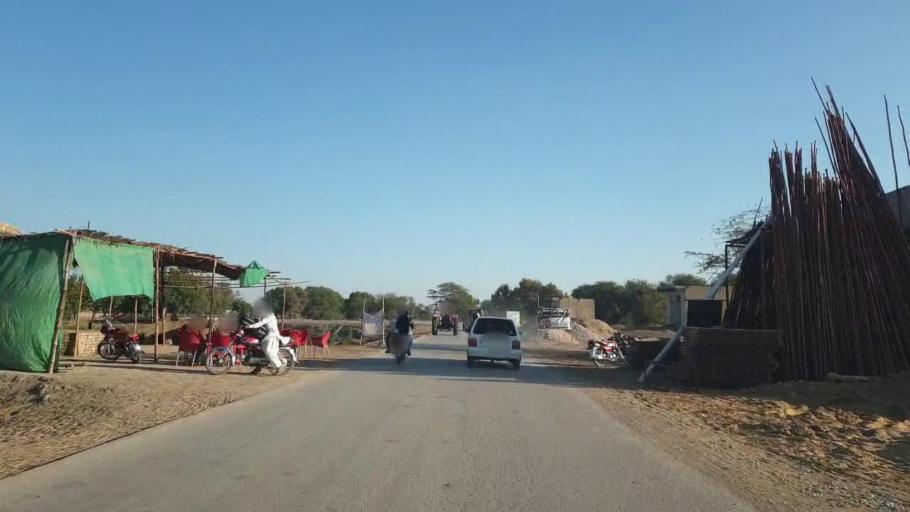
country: PK
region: Sindh
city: Dokri
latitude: 27.3661
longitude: 68.1126
